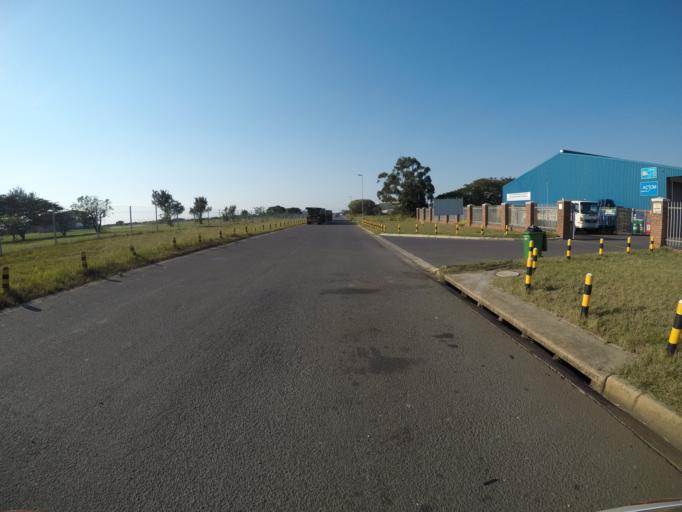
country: ZA
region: KwaZulu-Natal
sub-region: uThungulu District Municipality
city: Richards Bay
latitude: -28.7468
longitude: 32.0238
